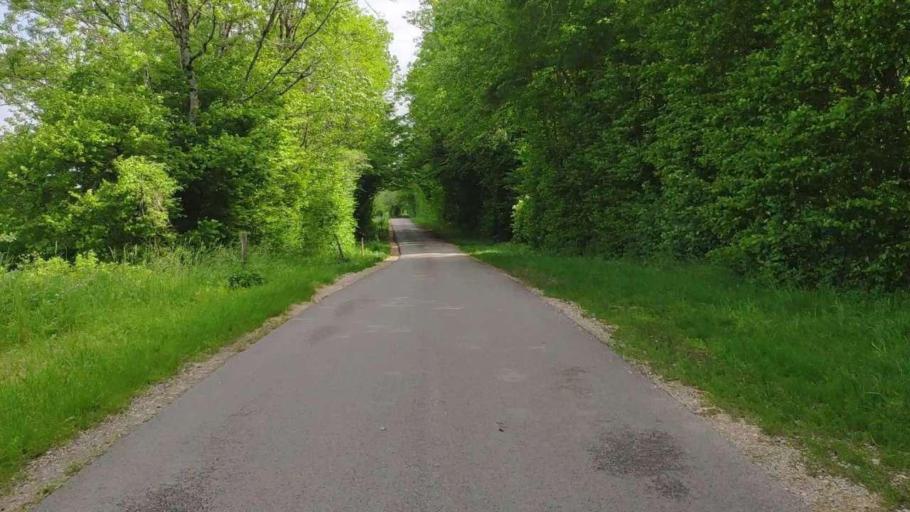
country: FR
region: Franche-Comte
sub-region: Departement du Jura
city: Poligny
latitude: 46.7830
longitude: 5.6661
